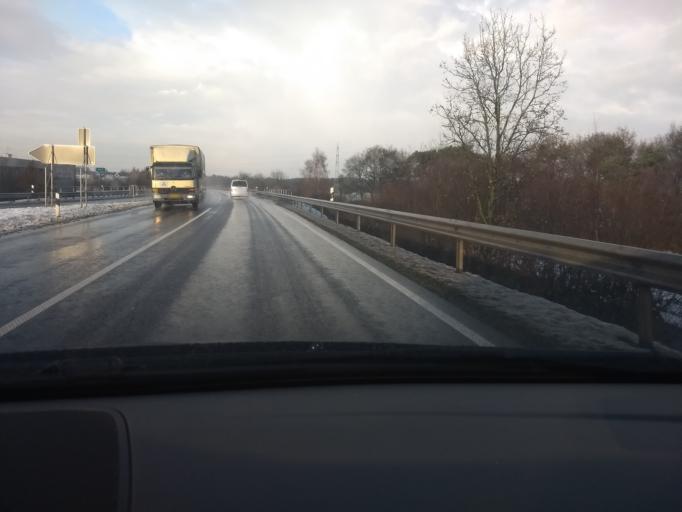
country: DE
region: Lower Saxony
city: Nordhorn
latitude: 52.4100
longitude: 7.0893
